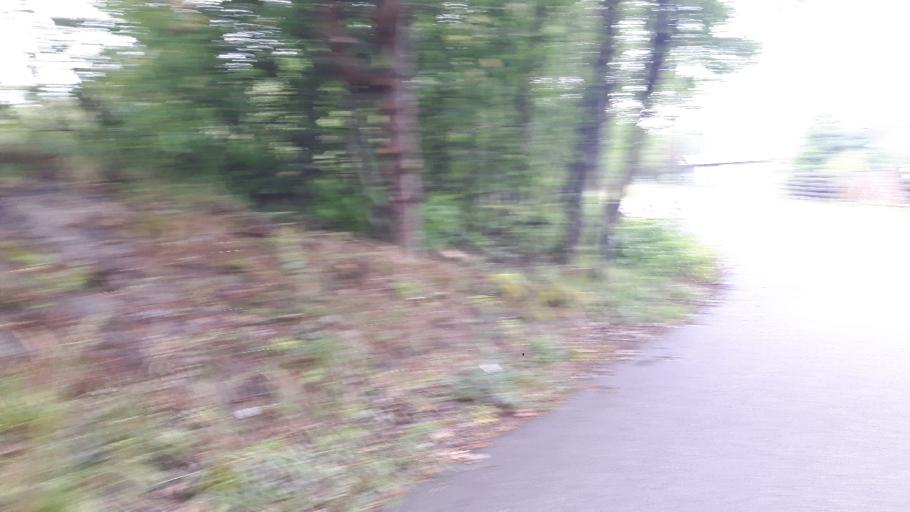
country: LT
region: Klaipedos apskritis
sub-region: Palanga
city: Sventoji
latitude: 56.0147
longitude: 21.0765
